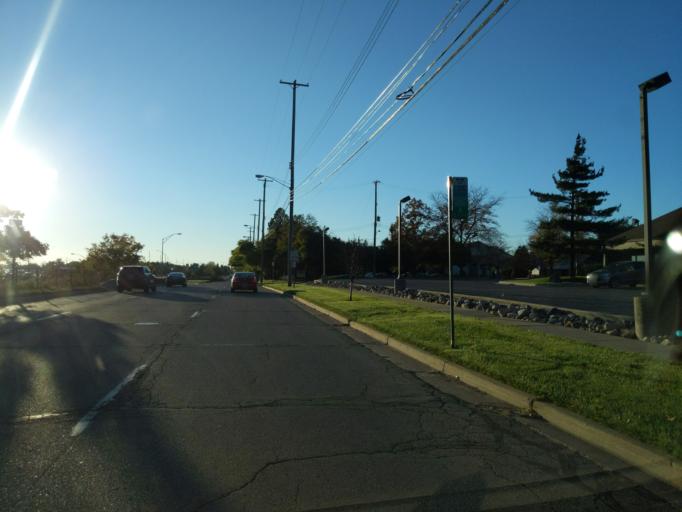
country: US
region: Michigan
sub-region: Ingham County
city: Lansing
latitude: 42.7264
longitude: -84.5607
